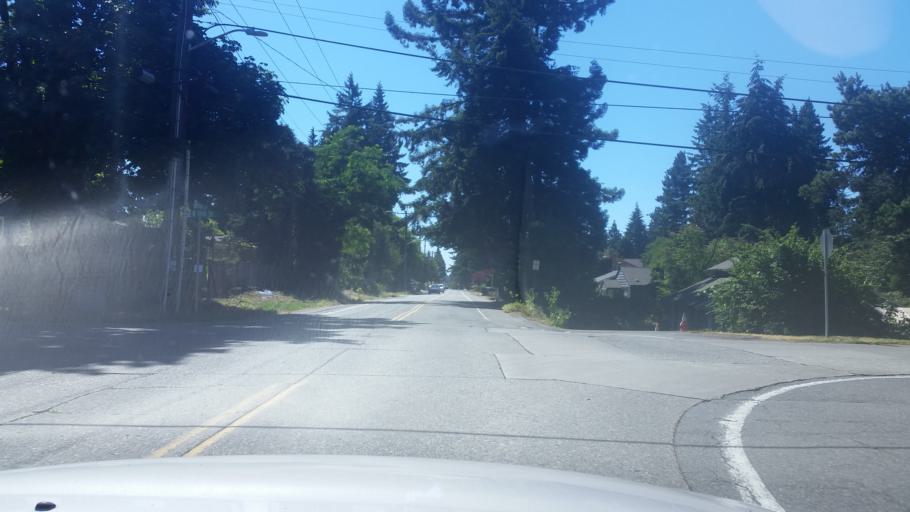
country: US
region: Washington
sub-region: King County
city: Shoreline
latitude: 47.7671
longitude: -122.3513
